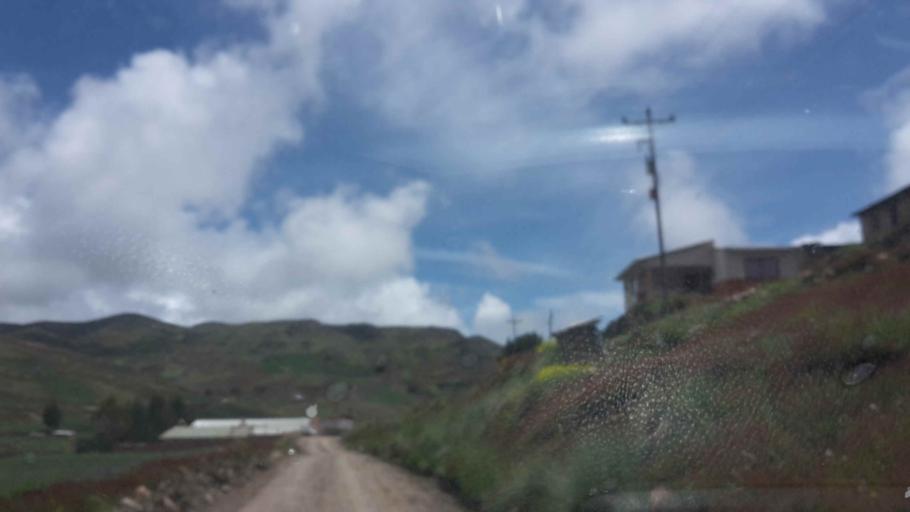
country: BO
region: Cochabamba
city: Cochabamba
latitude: -17.1949
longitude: -66.0814
